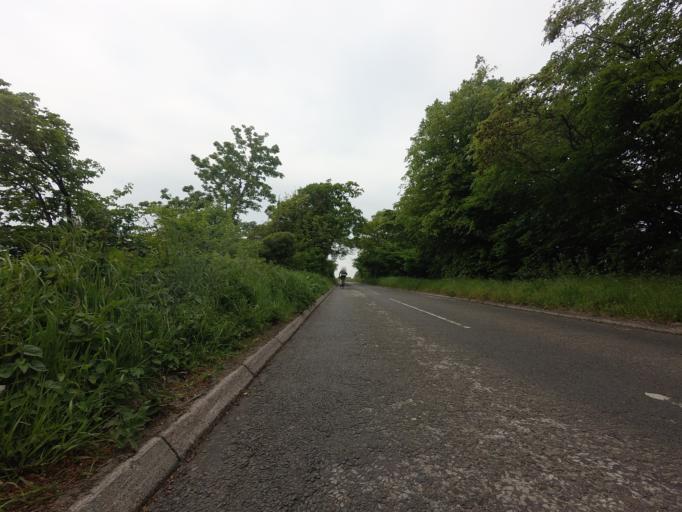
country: GB
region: Scotland
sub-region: Fife
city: Inverkeithing
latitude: 56.0446
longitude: -3.3971
